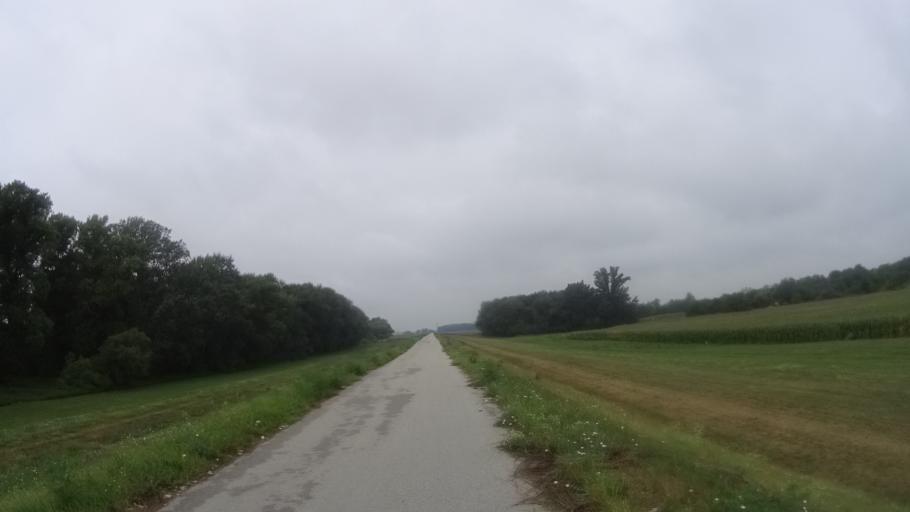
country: HU
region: Komarom-Esztergom
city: Almasfuzito
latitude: 47.7458
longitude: 18.2254
